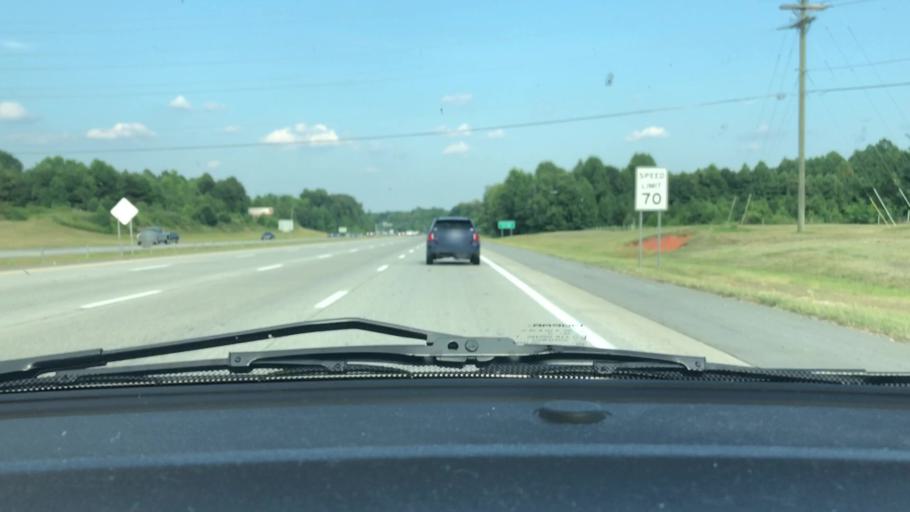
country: US
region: North Carolina
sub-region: Guilford County
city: Pleasant Garden
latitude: 35.9988
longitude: -79.7764
